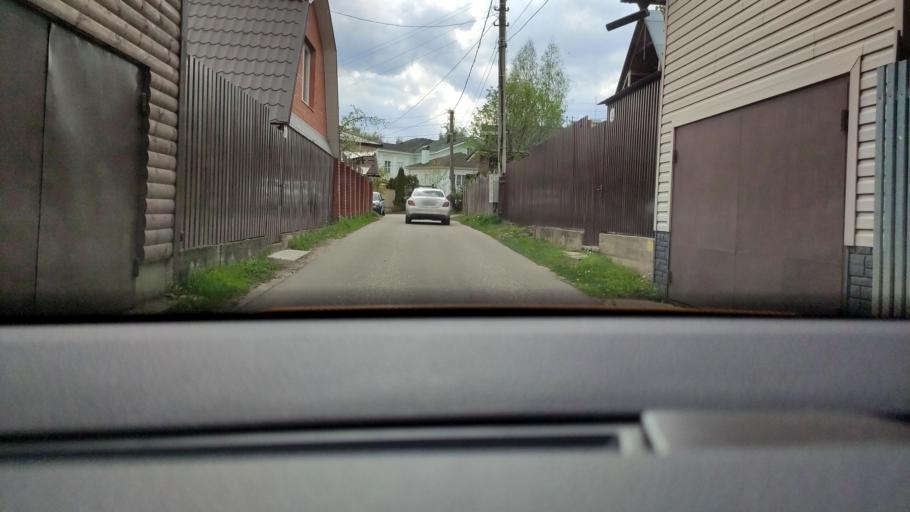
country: RU
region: Moskovskaya
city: Nikolina Gora
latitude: 55.7456
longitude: 37.0039
